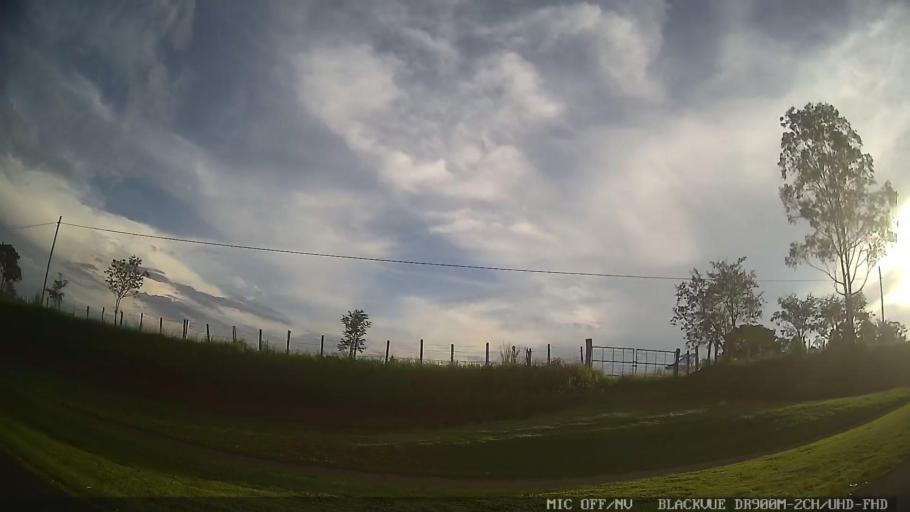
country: BR
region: Sao Paulo
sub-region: Tiete
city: Tiete
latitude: -23.1585
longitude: -47.6517
